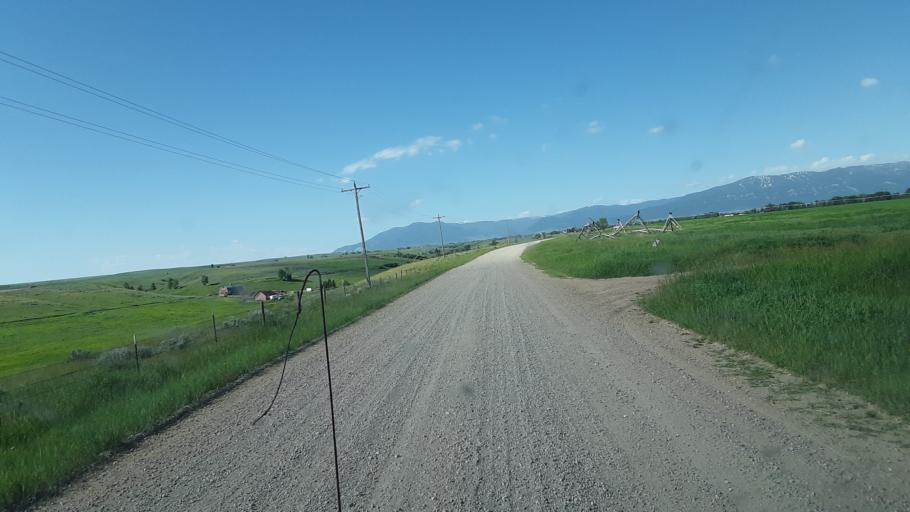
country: US
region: Montana
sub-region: Carbon County
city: Red Lodge
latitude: 45.3348
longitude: -109.1635
